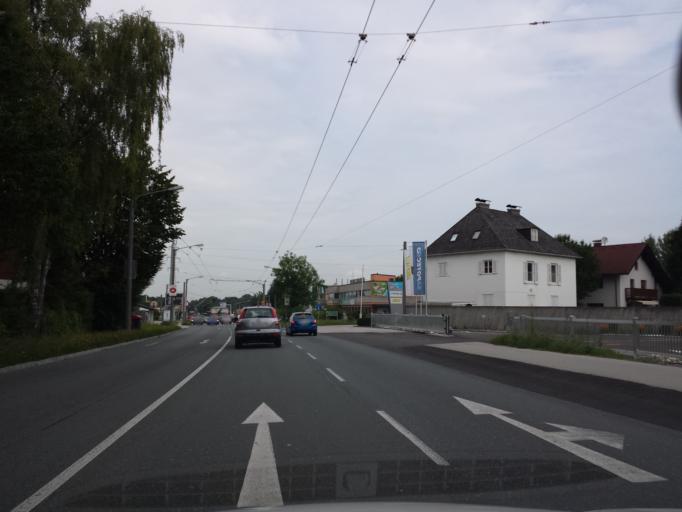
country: DE
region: Bavaria
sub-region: Upper Bavaria
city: Freilassing
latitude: 47.8309
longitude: 13.0016
